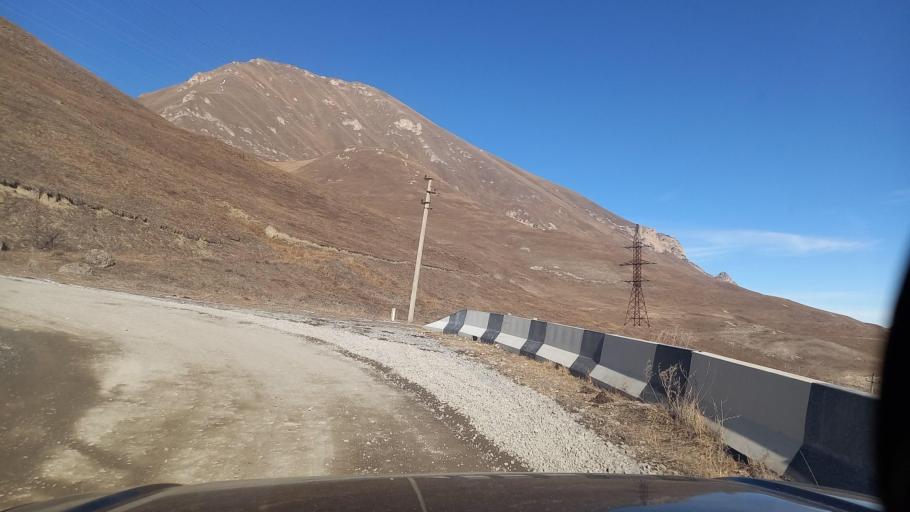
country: RU
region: North Ossetia
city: Verkhniy Fiagdon
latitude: 42.8348
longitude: 44.4893
